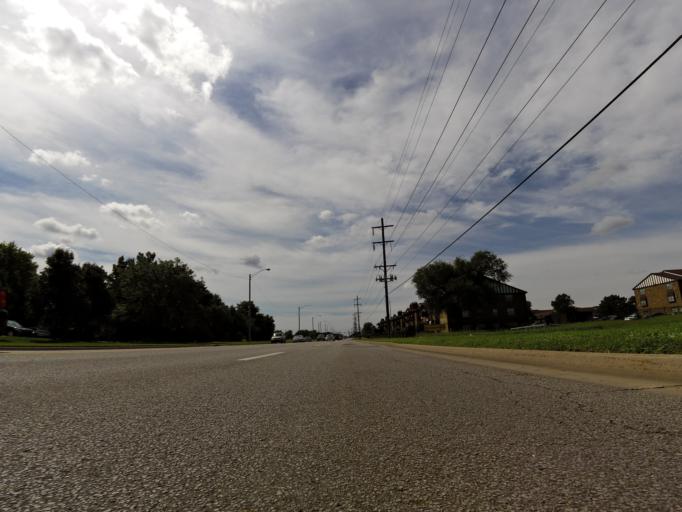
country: US
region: Kansas
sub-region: Sedgwick County
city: Bellaire
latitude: 37.7272
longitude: -97.2624
